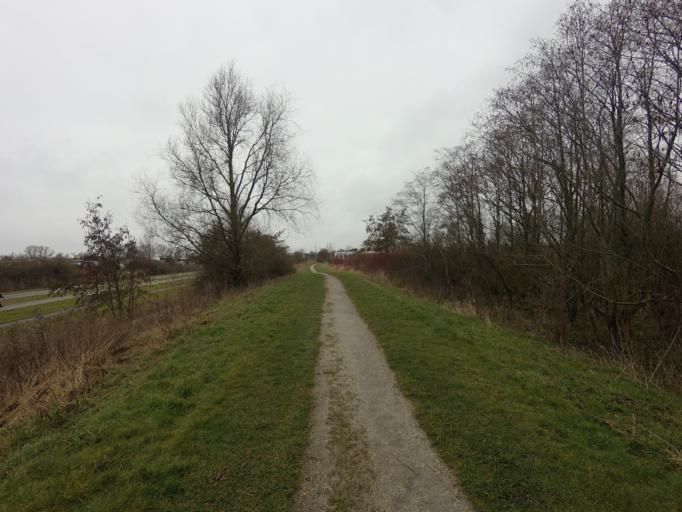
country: NL
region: Friesland
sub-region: Sudwest Fryslan
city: Makkum
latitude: 53.0504
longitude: 5.3892
